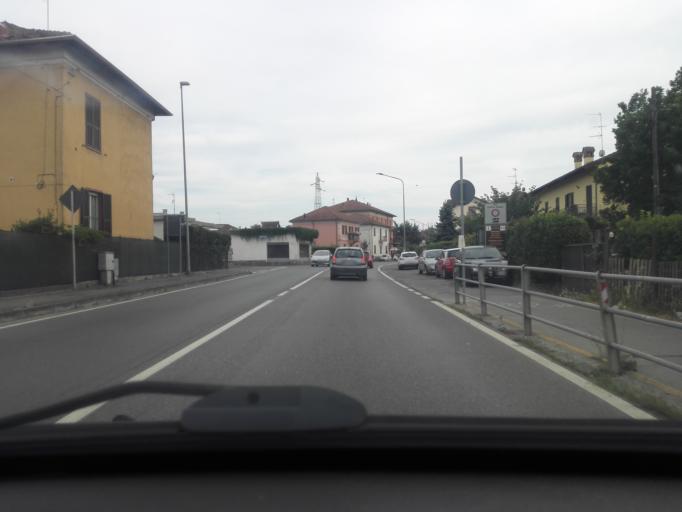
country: IT
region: Piedmont
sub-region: Provincia di Alessandria
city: Novi Ligure
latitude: 44.7734
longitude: 8.7899
